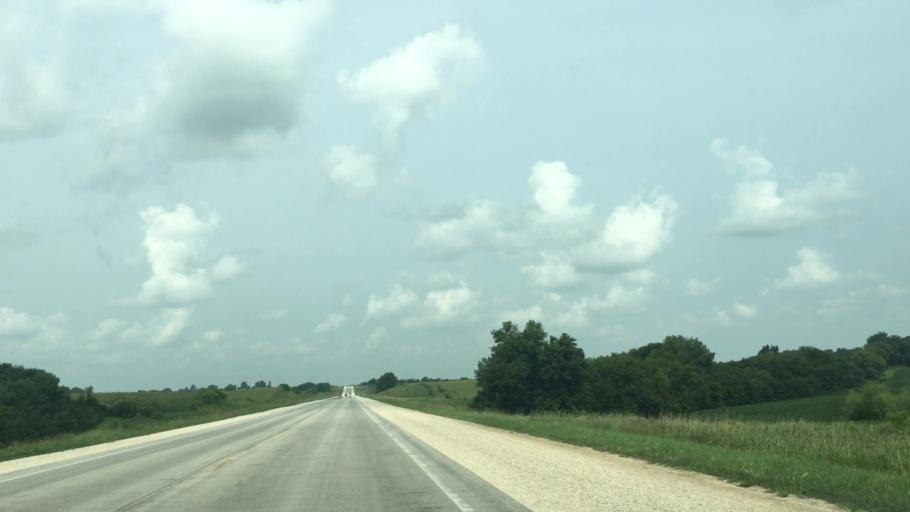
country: US
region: Iowa
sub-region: Winneshiek County
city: Decorah
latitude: 43.3702
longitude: -91.8091
